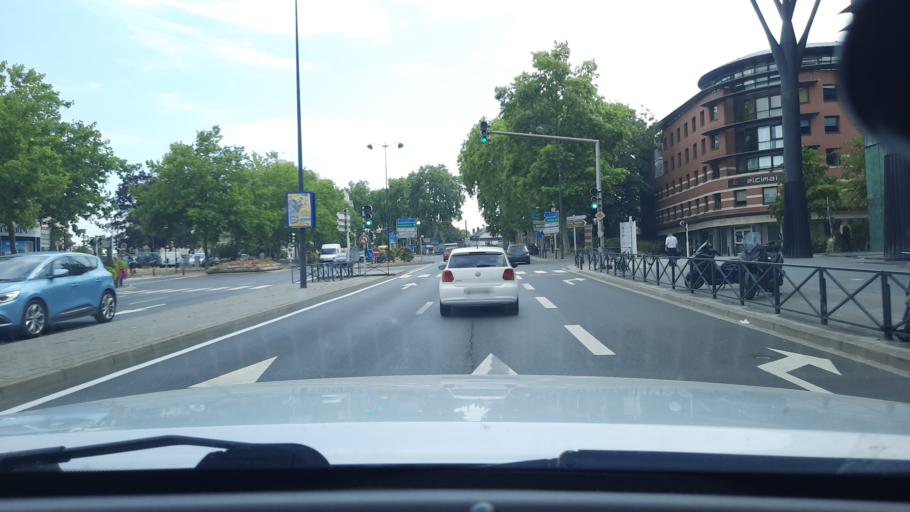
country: FR
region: Ile-de-France
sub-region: Departement de Seine-et-Marne
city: Dammarie-les-Lys
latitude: 48.5270
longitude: 2.6533
